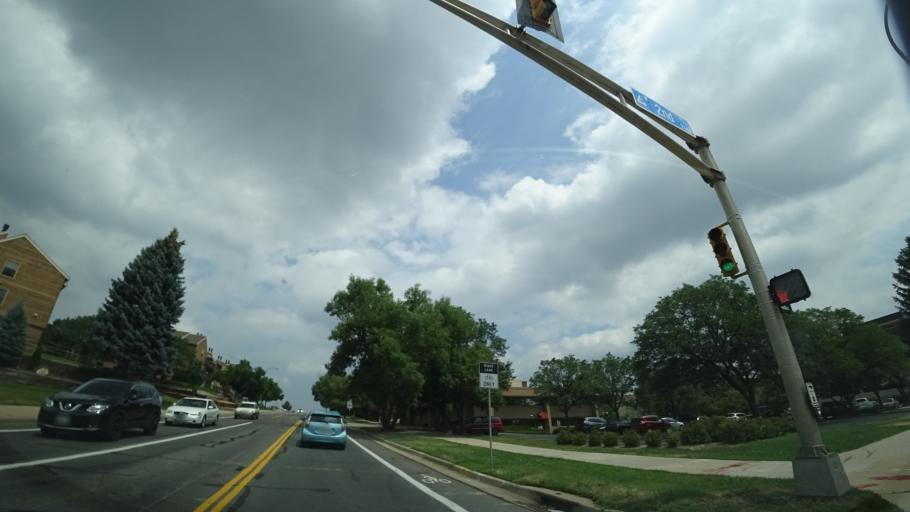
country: US
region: Colorado
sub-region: Jefferson County
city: West Pleasant View
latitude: 39.7188
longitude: -105.1352
